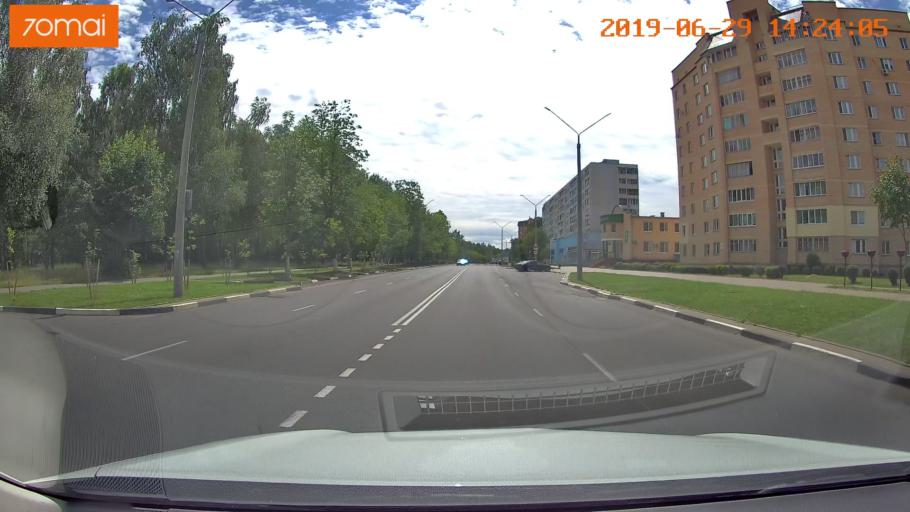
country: BY
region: Minsk
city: Salihorsk
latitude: 52.7823
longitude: 27.5512
